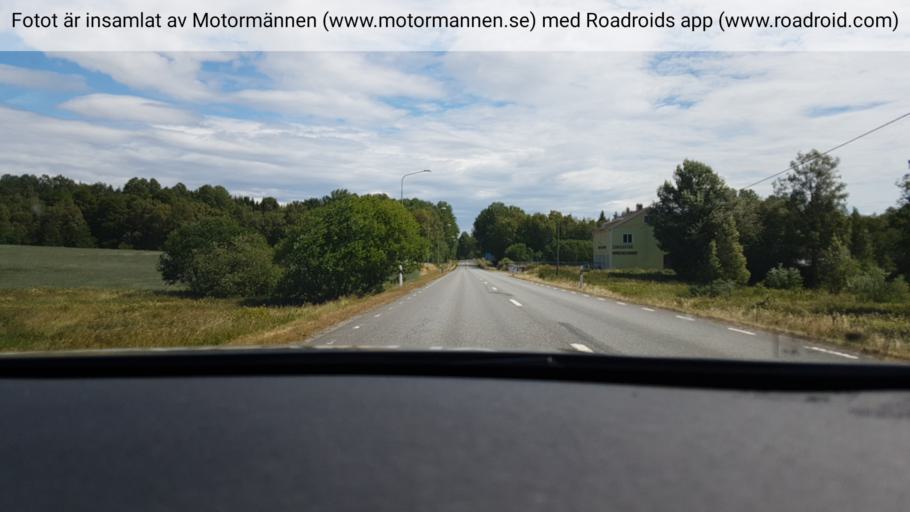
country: SE
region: Joenkoeping
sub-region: Aneby Kommun
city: Aneby
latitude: 57.9752
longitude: 14.7891
